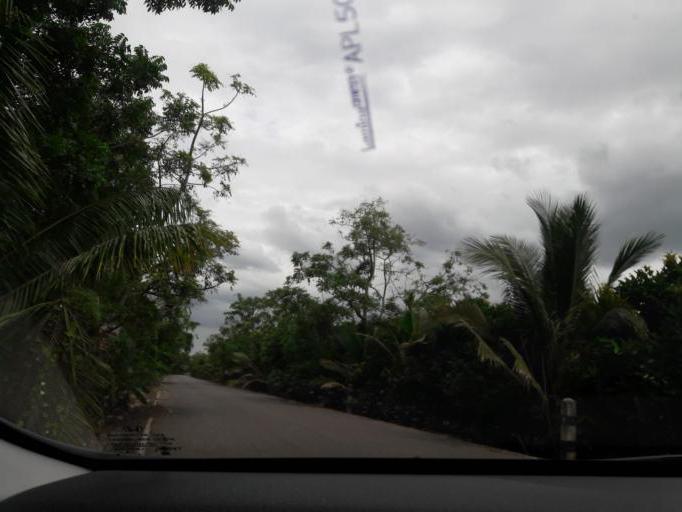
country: TH
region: Ratchaburi
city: Damnoen Saduak
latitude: 13.5657
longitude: 99.9839
